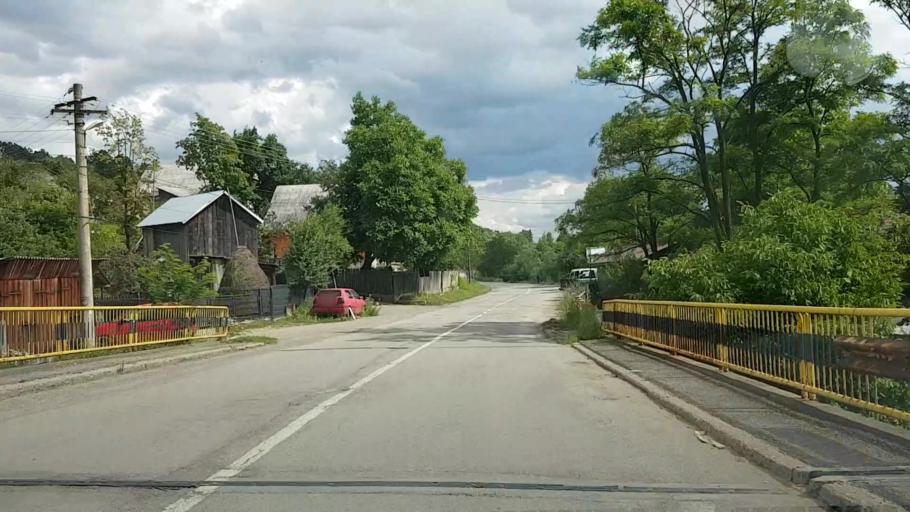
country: RO
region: Neamt
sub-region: Comuna Hangu
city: Hangu
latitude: 47.0440
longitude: 26.0540
